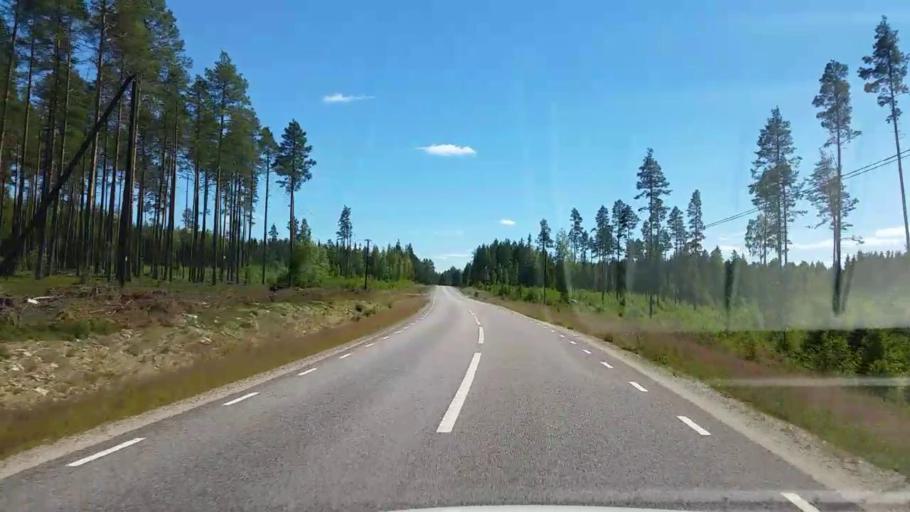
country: SE
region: Gaevleborg
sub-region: Ovanakers Kommun
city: Edsbyn
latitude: 61.4586
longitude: 15.7014
